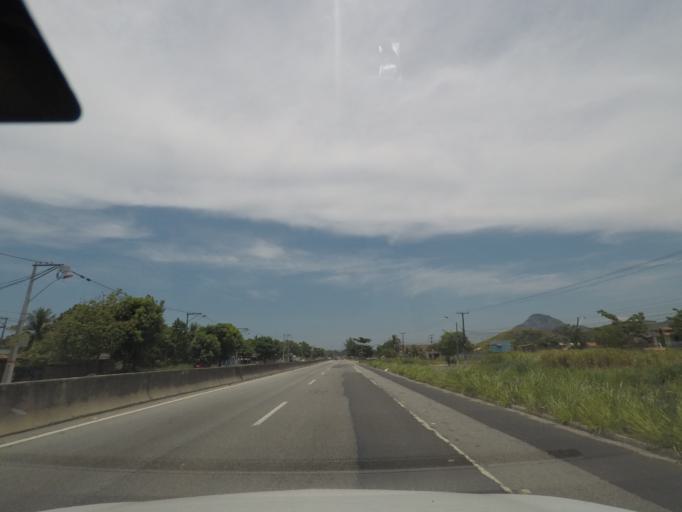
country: BR
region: Rio de Janeiro
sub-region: Marica
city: Marica
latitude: -22.9240
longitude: -42.8622
